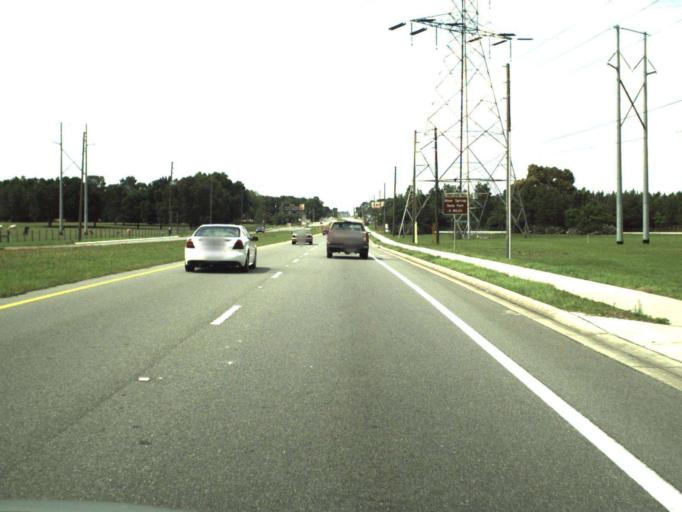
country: US
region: Florida
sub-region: Marion County
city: Silver Springs Shores
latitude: 29.1426
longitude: -82.0535
